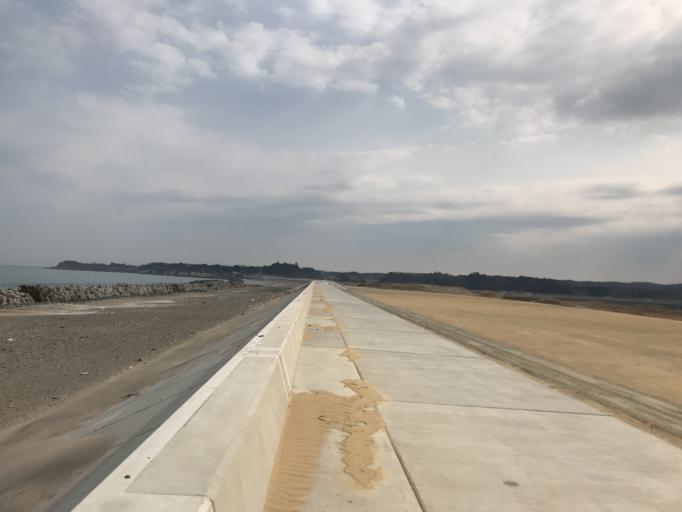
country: JP
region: Miyagi
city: Marumori
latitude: 37.7766
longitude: 140.9877
